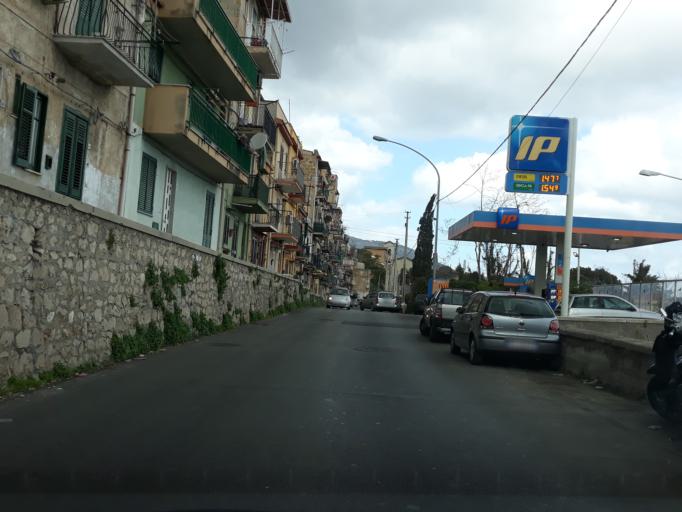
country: IT
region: Sicily
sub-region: Palermo
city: Monreale
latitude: 38.1068
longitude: 13.3096
